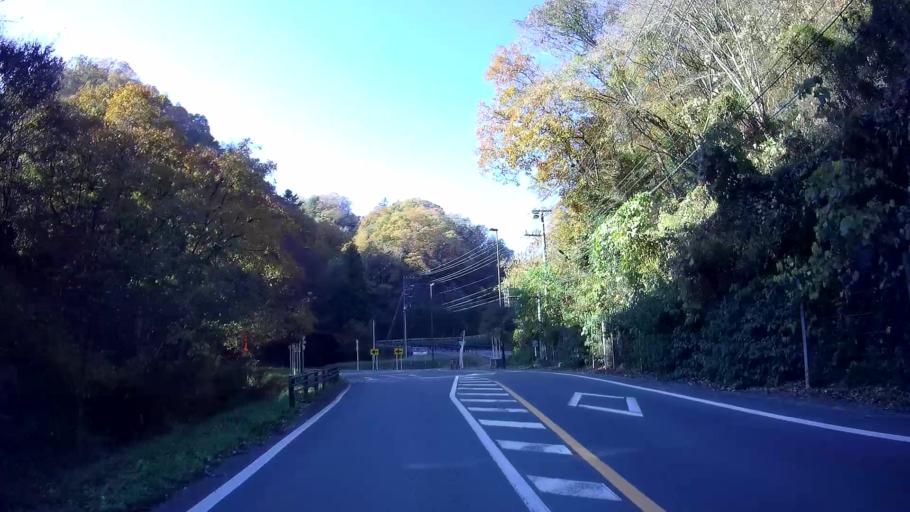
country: JP
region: Yamanashi
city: Uenohara
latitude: 35.6024
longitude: 139.1224
